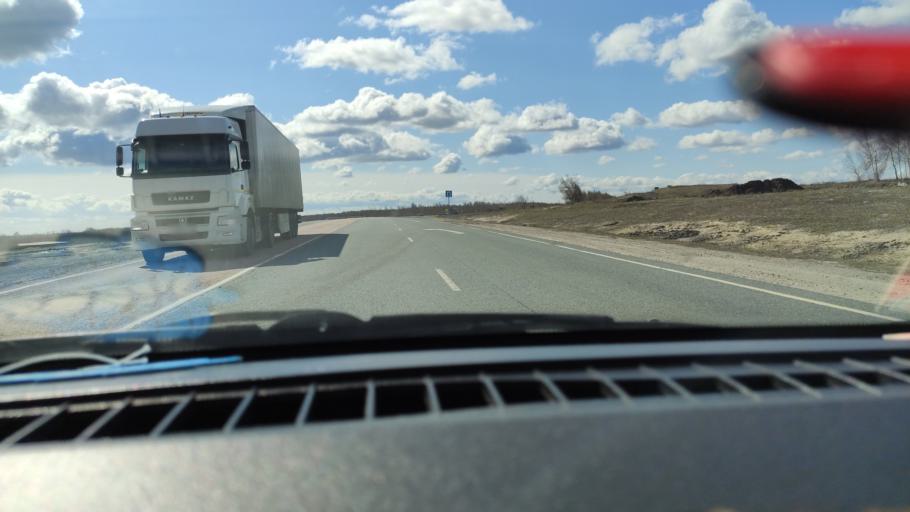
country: RU
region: Samara
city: Syzran'
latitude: 52.9531
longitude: 48.3069
